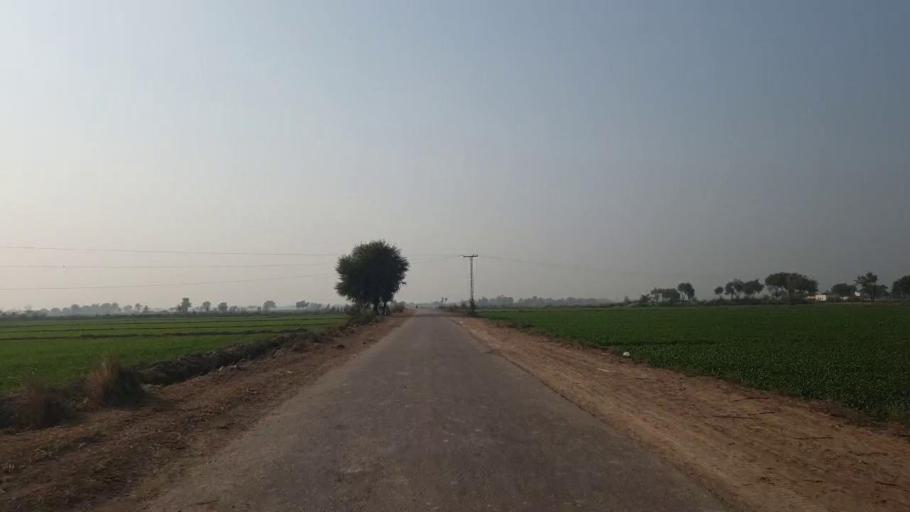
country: PK
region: Sindh
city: Shahdadpur
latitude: 25.9658
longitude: 68.5638
